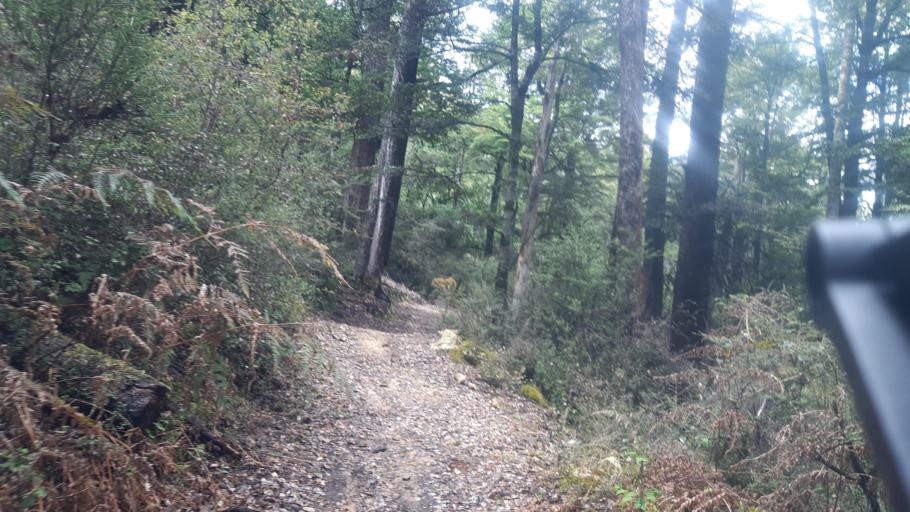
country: NZ
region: Tasman
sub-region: Tasman District
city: Wakefield
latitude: -41.7594
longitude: 172.8056
